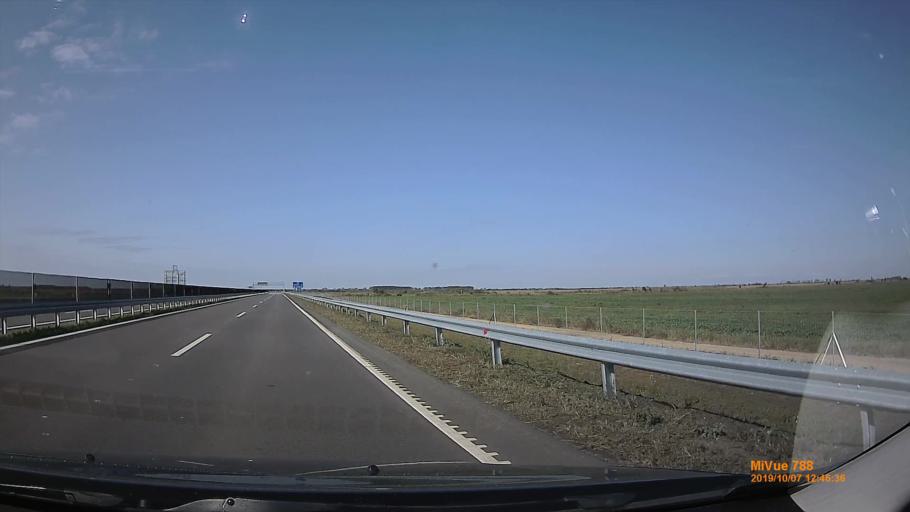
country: HU
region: Jasz-Nagykun-Szolnok
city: Kunszentmarton
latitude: 46.8746
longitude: 20.2586
